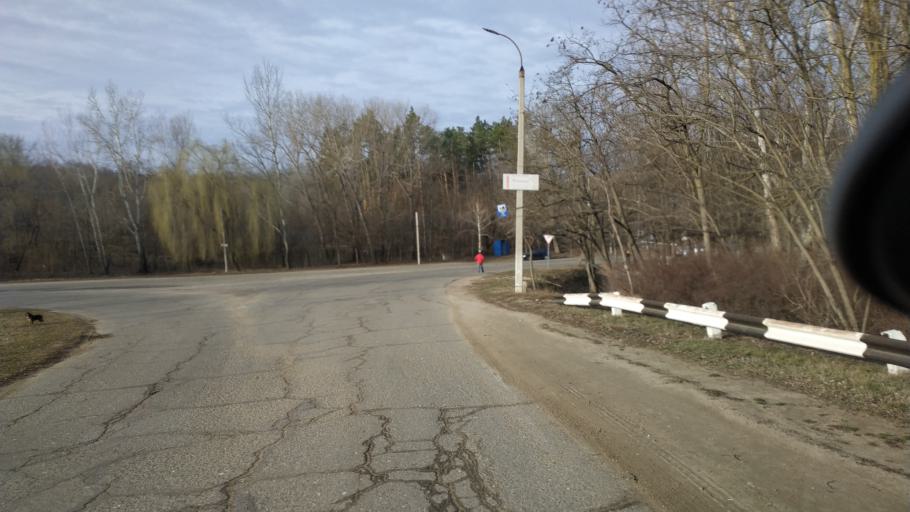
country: MD
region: Chisinau
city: Vadul lui Voda
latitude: 47.0856
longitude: 29.0877
